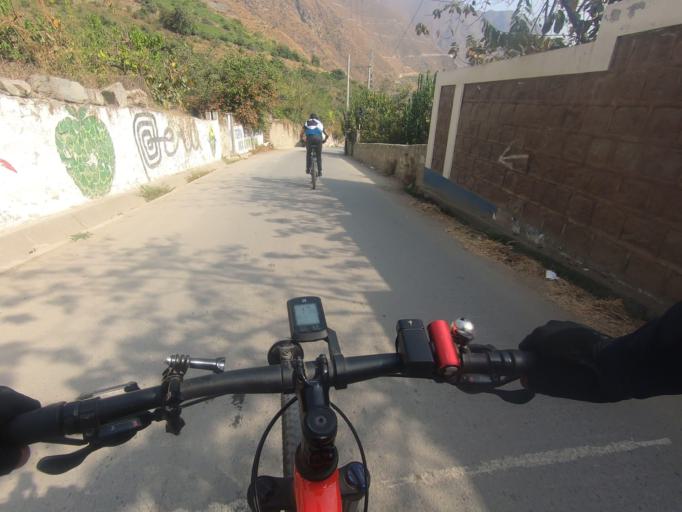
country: PE
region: Lima
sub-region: Provincia de Huarochiri
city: Callahuanca
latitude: -11.8276
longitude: -76.6160
